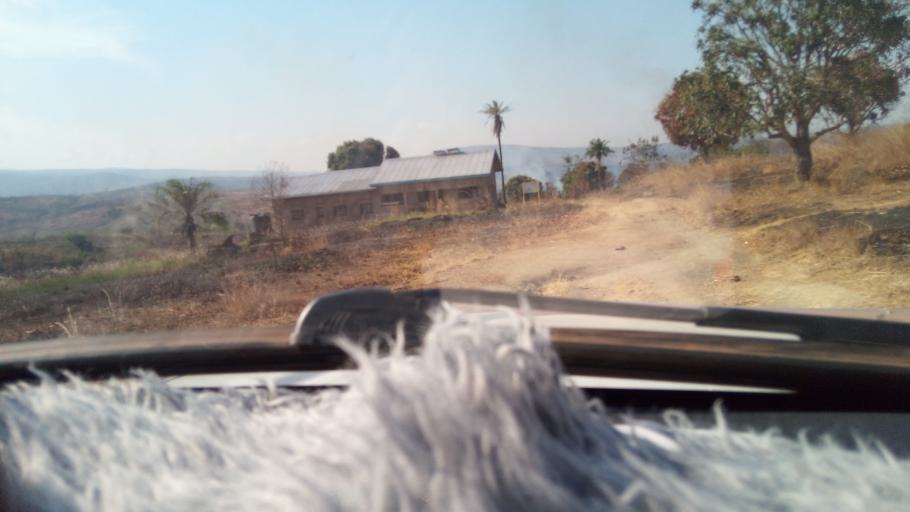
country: CD
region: Katanga
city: Kalemie
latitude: -5.9032
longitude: 29.1262
